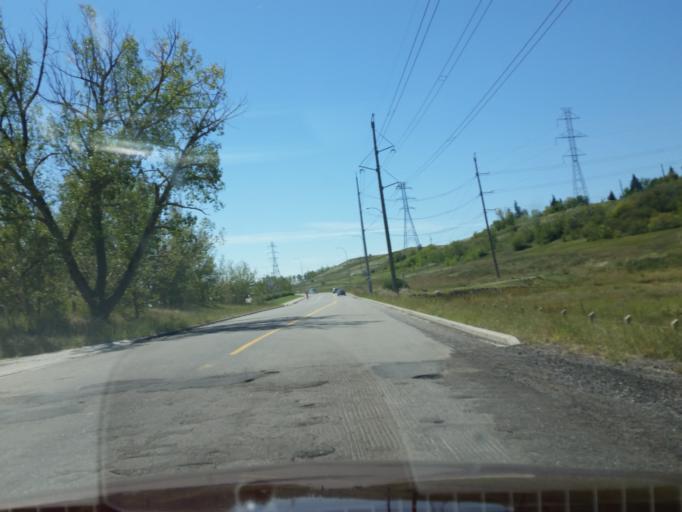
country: CA
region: Alberta
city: Calgary
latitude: 51.0563
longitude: -114.0266
